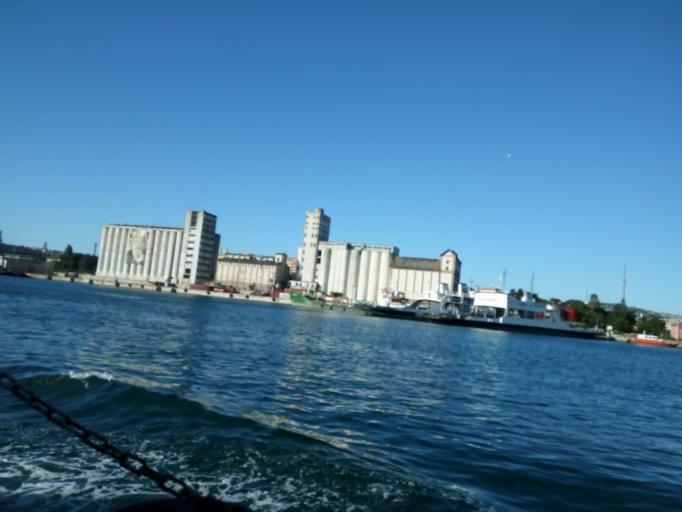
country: TR
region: Istanbul
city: UEskuedar
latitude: 40.9962
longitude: 29.0166
